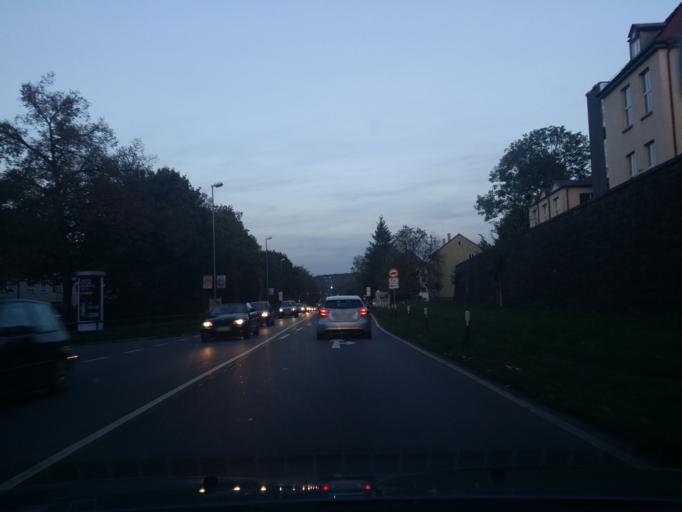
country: DE
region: Baden-Wuerttemberg
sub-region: Tuebingen Region
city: Tuebingen
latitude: 48.5106
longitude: 9.0648
